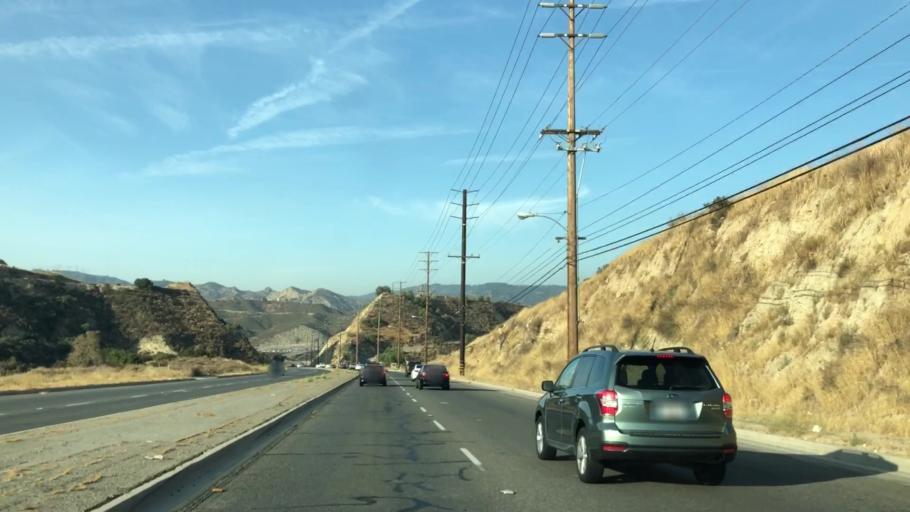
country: US
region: California
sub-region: Los Angeles County
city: Santa Clarita
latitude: 34.3903
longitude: -118.4887
